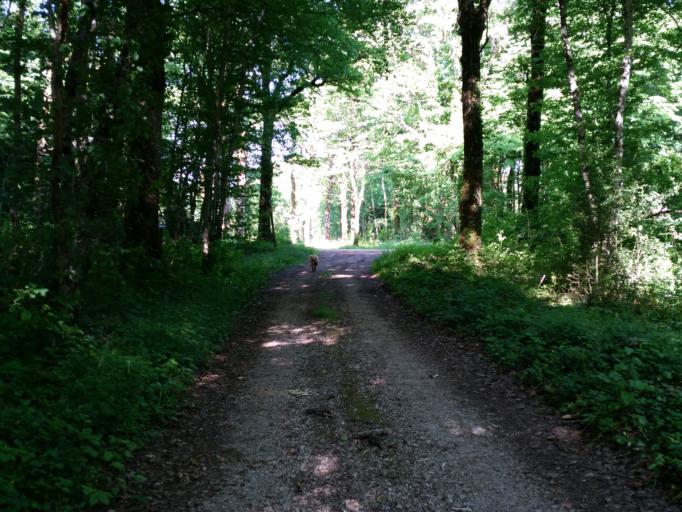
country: FR
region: Franche-Comte
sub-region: Departement du Doubs
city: Quingey
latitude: 47.0479
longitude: 5.9812
